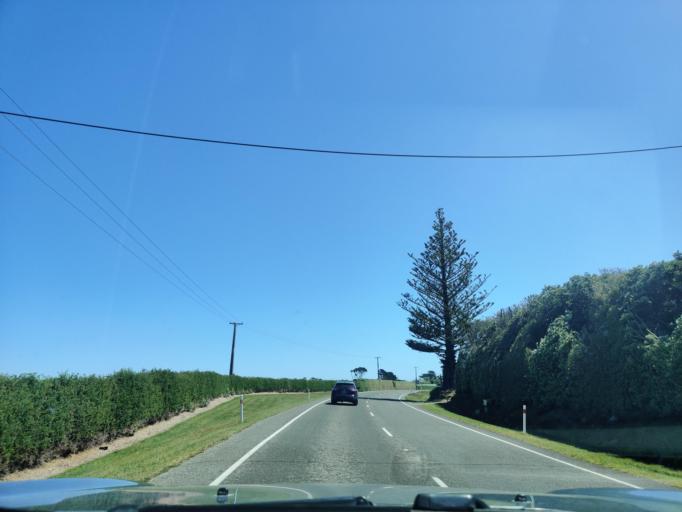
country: NZ
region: Taranaki
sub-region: South Taranaki District
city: Opunake
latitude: -39.5461
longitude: 174.0630
